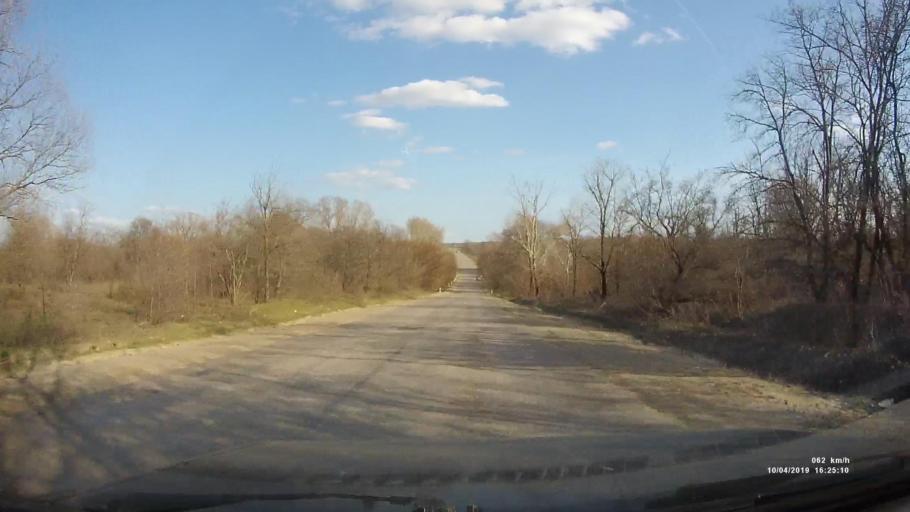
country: RU
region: Rostov
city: Staraya Stanitsa
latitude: 48.2947
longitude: 40.3210
